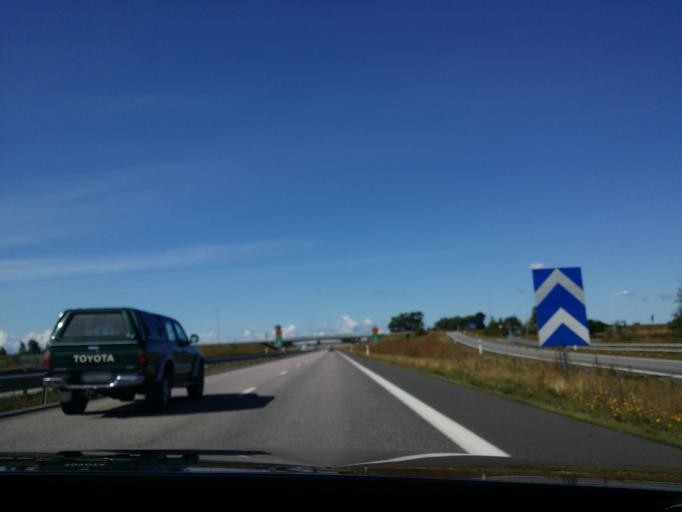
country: SE
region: Skane
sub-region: Kristianstads Kommun
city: Fjalkinge
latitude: 56.0344
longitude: 14.2697
